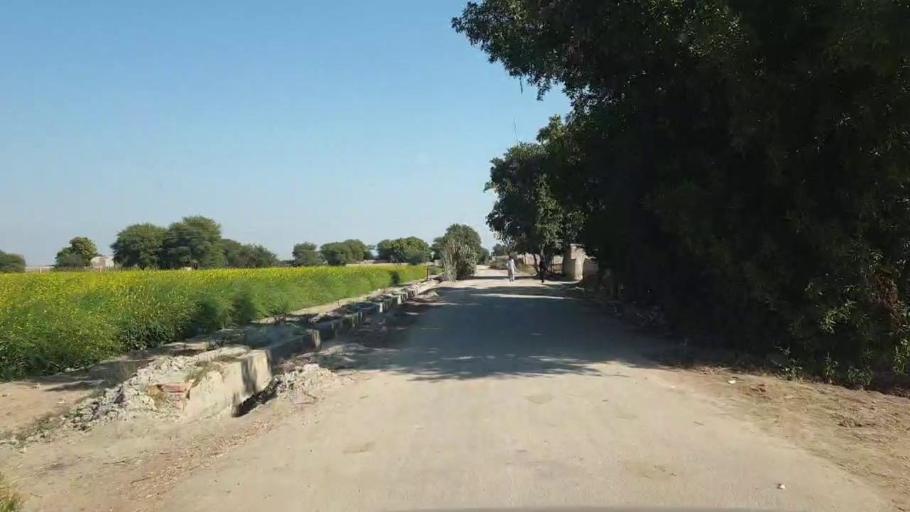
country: PK
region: Sindh
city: Shahpur Chakar
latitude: 26.1080
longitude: 68.6538
